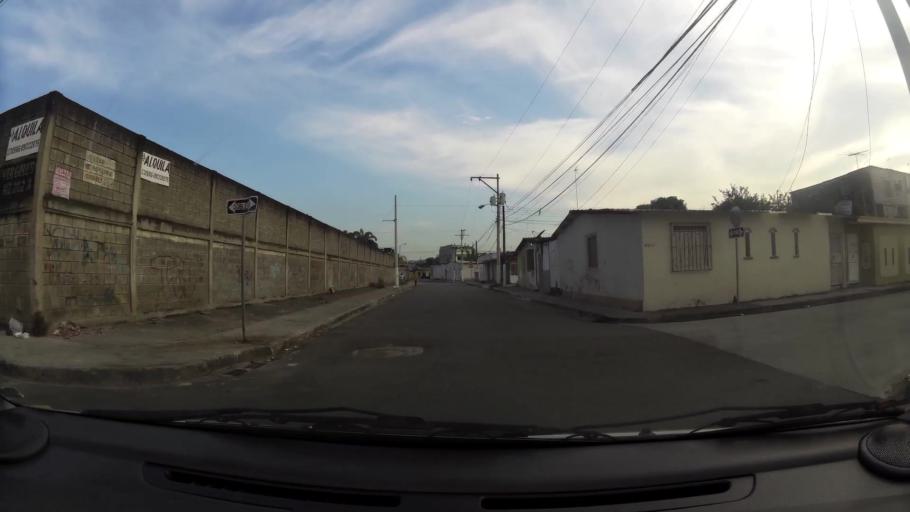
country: EC
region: Guayas
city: Eloy Alfaro
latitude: -2.0955
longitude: -79.9077
